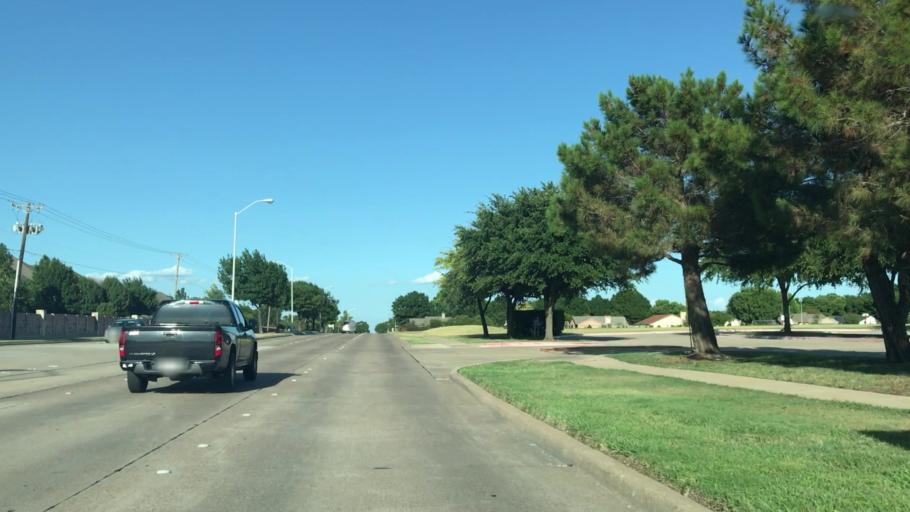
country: US
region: Texas
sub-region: Collin County
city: Plano
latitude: 33.0715
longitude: -96.7359
